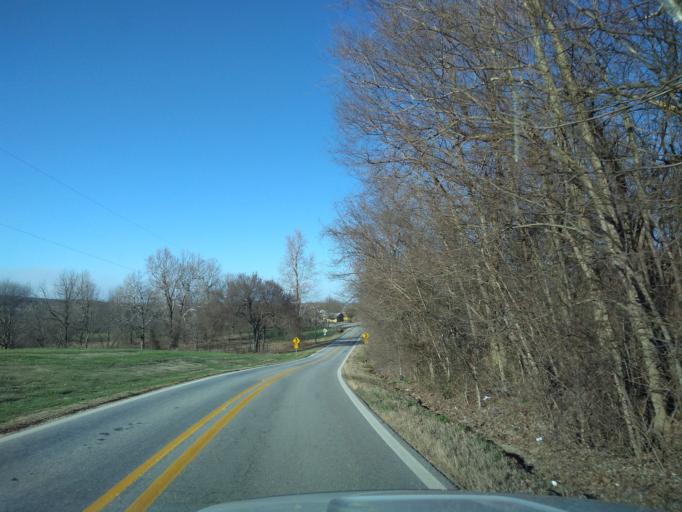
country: US
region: Arkansas
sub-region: Washington County
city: Lincoln
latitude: 35.9438
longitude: -94.3766
